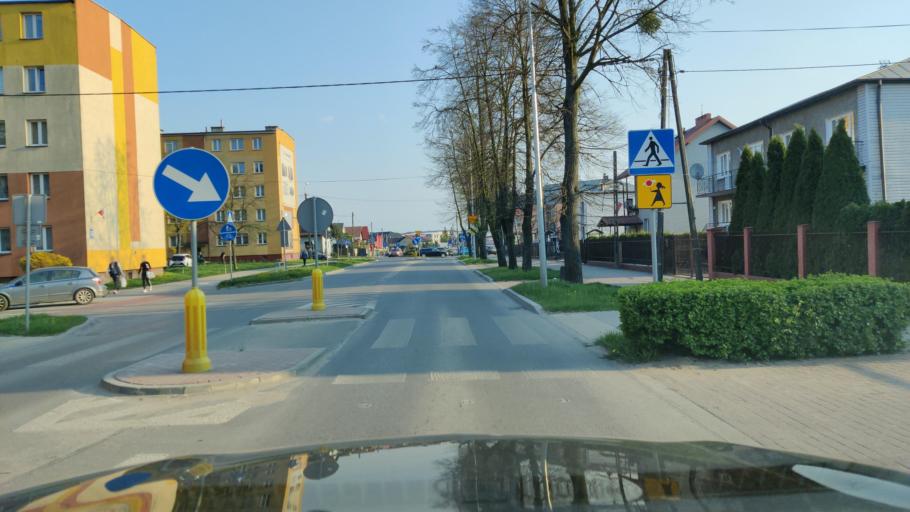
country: PL
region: Masovian Voivodeship
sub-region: Powiat pultuski
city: Pultusk
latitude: 52.7038
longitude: 21.0762
